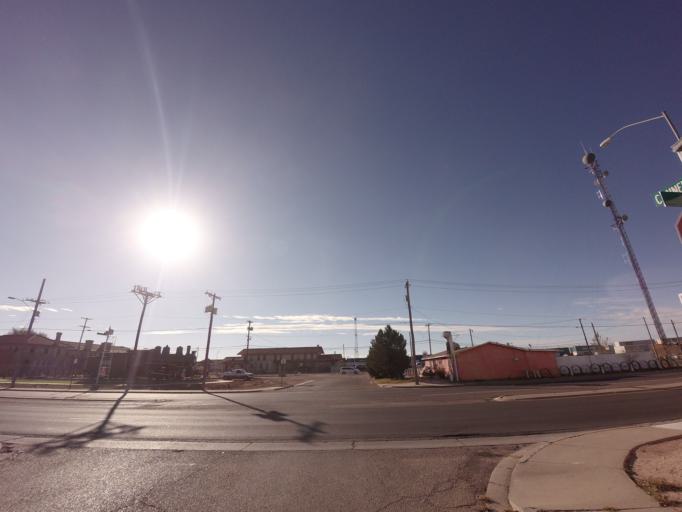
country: US
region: New Mexico
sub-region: Curry County
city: Clovis
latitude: 34.3988
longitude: -103.2080
